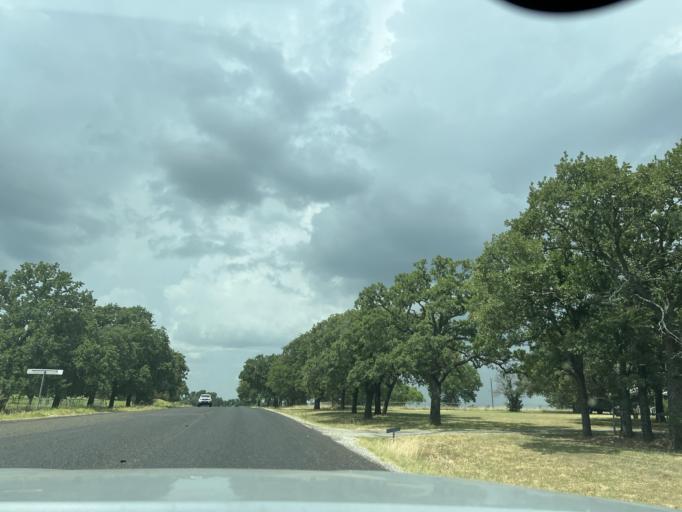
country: US
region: Texas
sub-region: Wise County
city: Decatur
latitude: 33.1881
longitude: -97.6153
